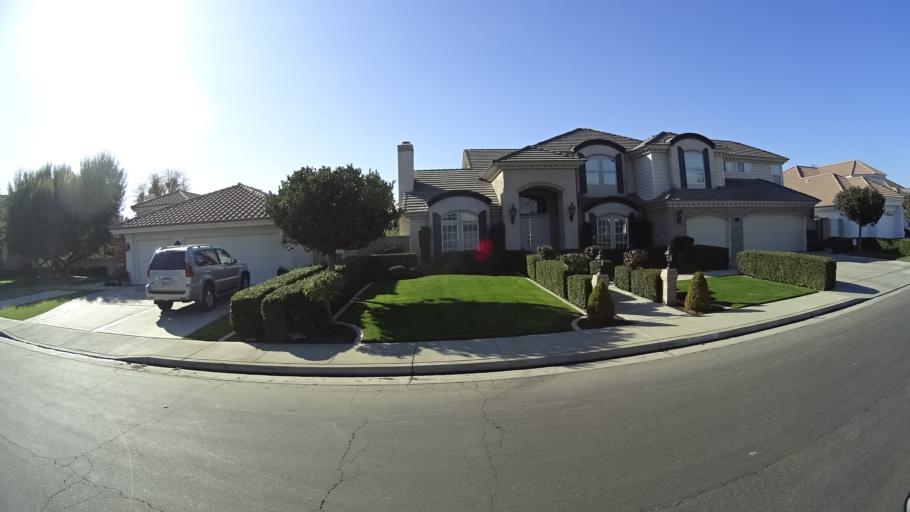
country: US
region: California
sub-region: Kern County
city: Greenacres
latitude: 35.3384
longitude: -119.1233
